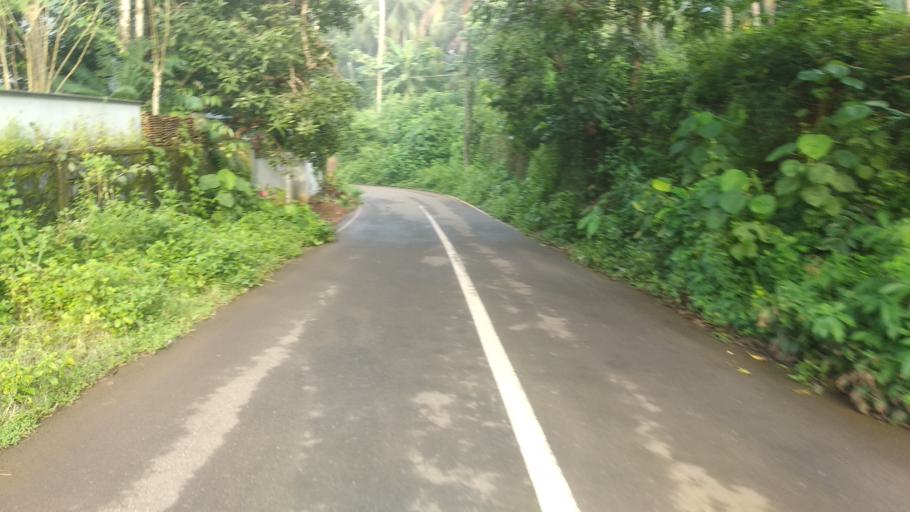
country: IN
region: Kerala
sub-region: Malappuram
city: Malappuram
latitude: 10.9900
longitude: 76.0467
